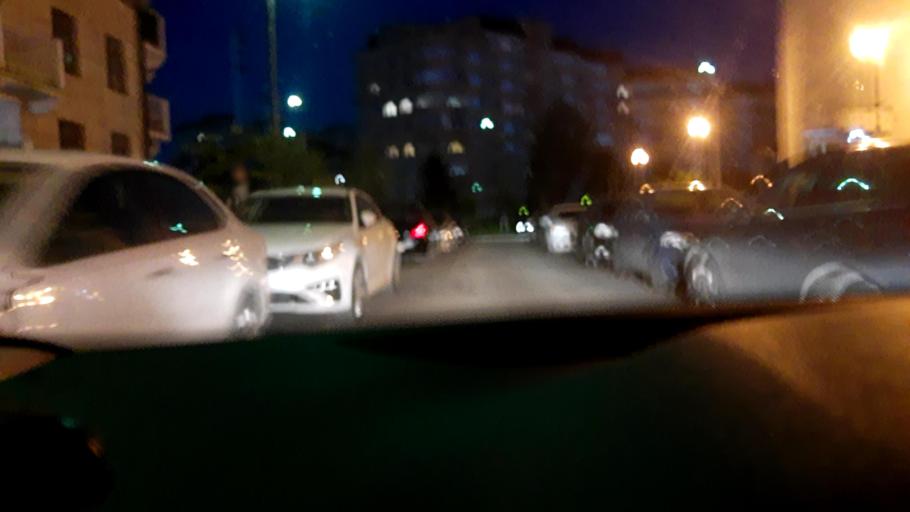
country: RU
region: Moskovskaya
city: Opalikha
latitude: 55.8334
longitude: 37.2395
